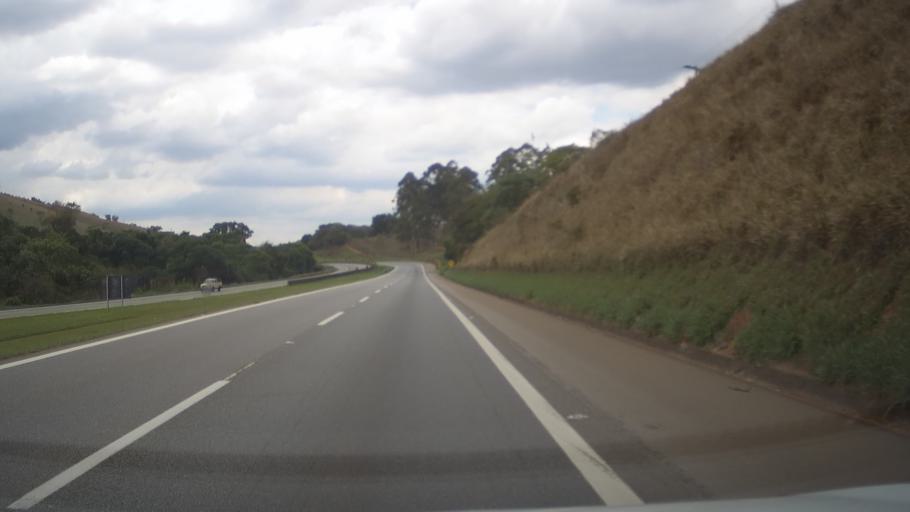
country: BR
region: Minas Gerais
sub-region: Tres Coracoes
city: Tres Coracoes
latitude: -21.5246
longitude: -45.2256
